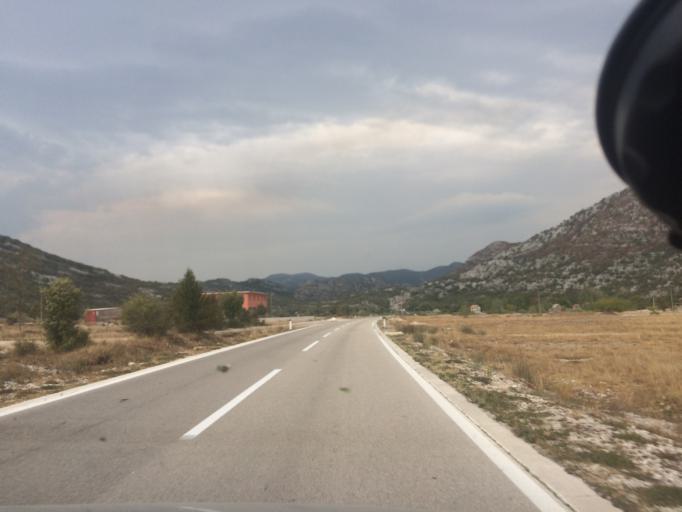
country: ME
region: Kotor
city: Risan
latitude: 42.6148
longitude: 18.6820
